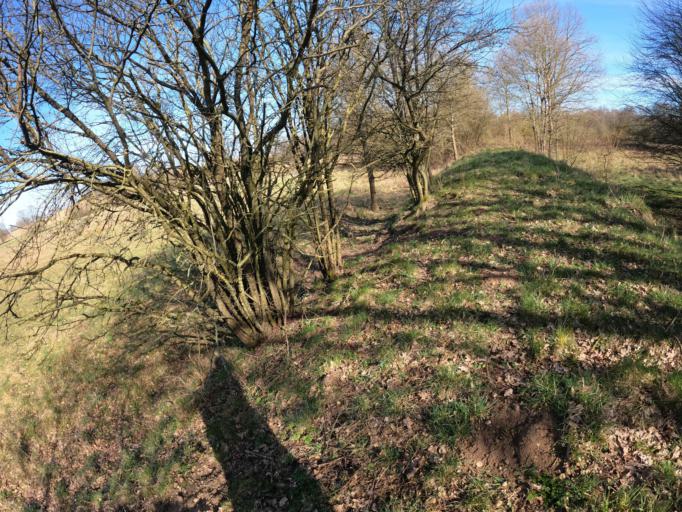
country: PL
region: West Pomeranian Voivodeship
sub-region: Powiat gryficki
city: Brojce
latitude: 53.9229
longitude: 15.3059
